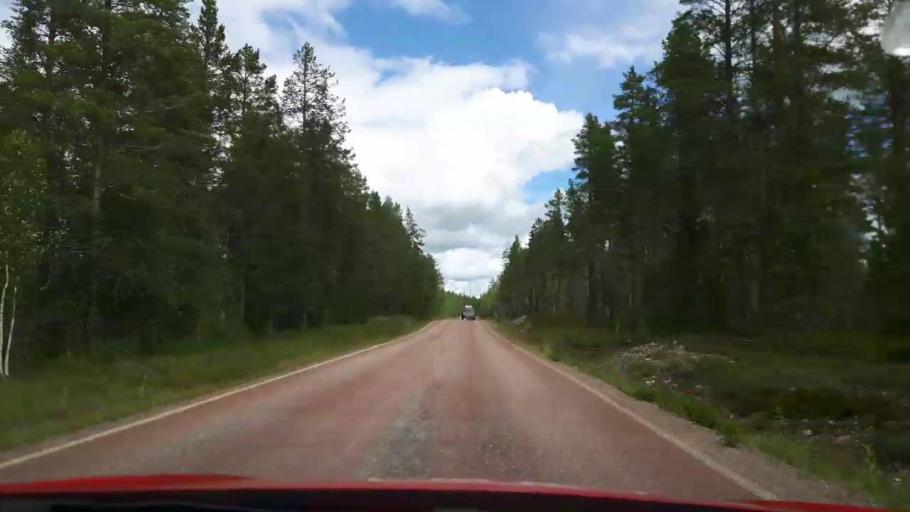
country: NO
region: Hedmark
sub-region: Trysil
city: Innbygda
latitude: 61.9020
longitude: 12.9919
